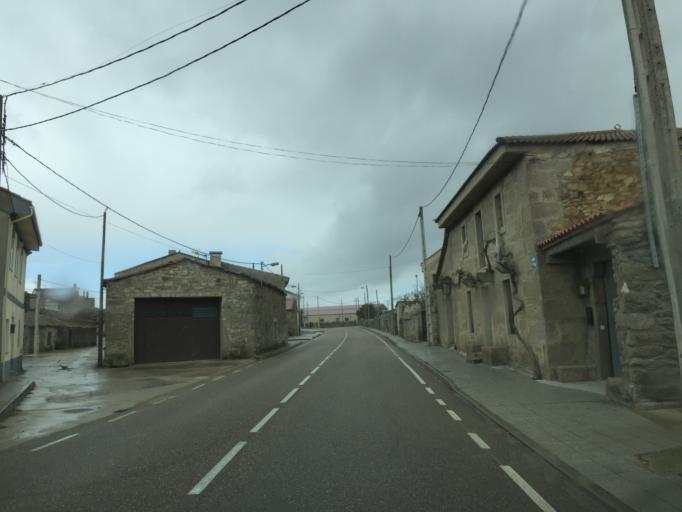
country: ES
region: Castille and Leon
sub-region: Provincia de Zamora
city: Villalcampo
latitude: 41.5214
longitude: -6.0492
